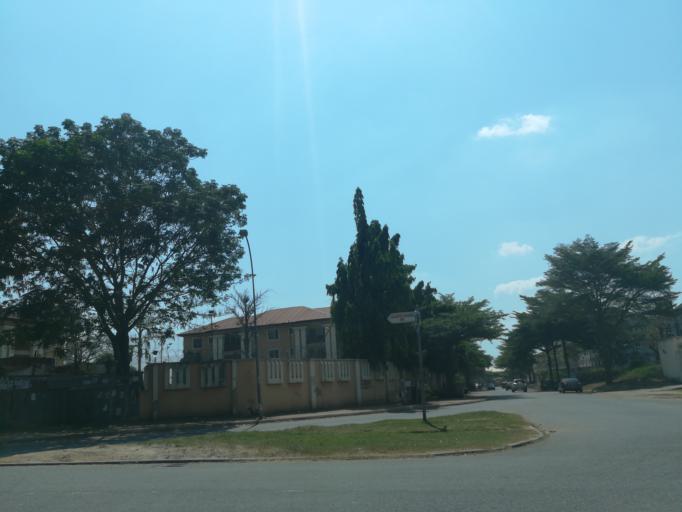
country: NG
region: Abuja Federal Capital Territory
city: Abuja
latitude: 9.0716
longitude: 7.4438
